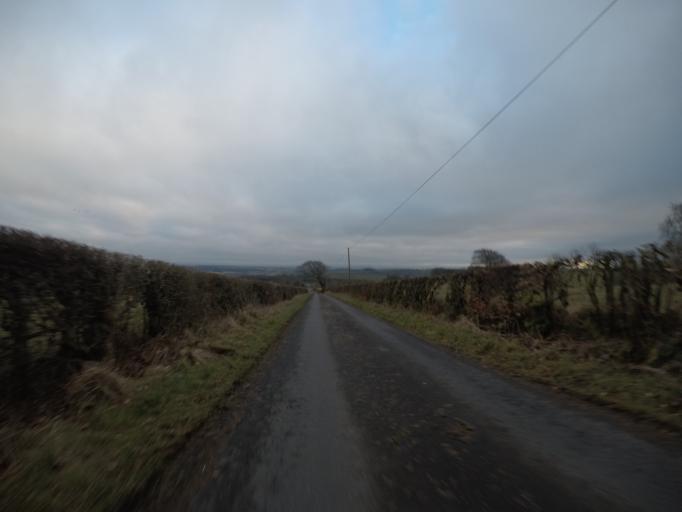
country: GB
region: Scotland
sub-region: North Ayrshire
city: Dalry
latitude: 55.7188
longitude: -4.7585
